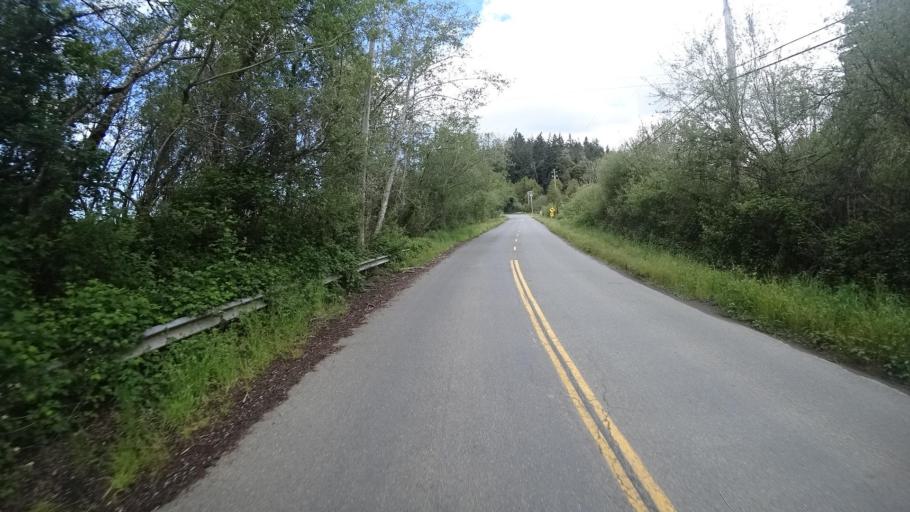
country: US
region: California
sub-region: Humboldt County
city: Blue Lake
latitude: 40.8984
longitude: -124.0092
